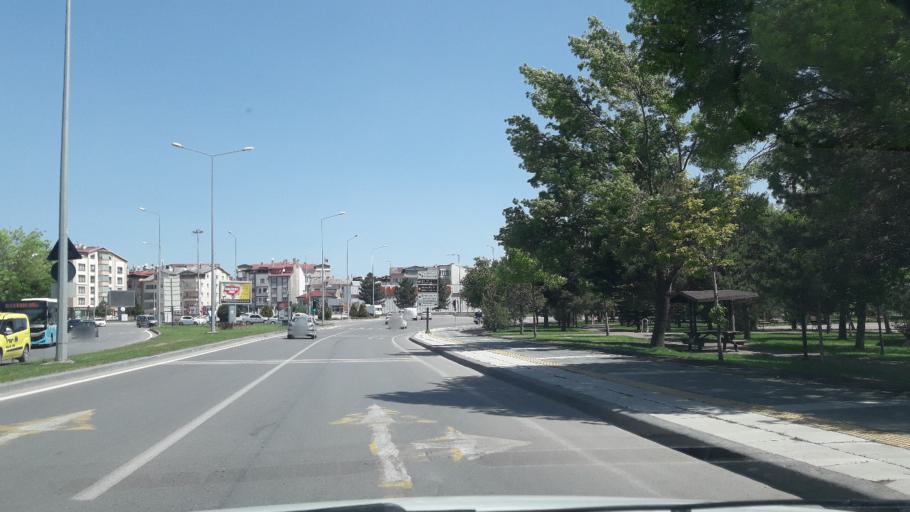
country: TR
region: Sivas
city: Sivas
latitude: 39.7382
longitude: 37.0160
